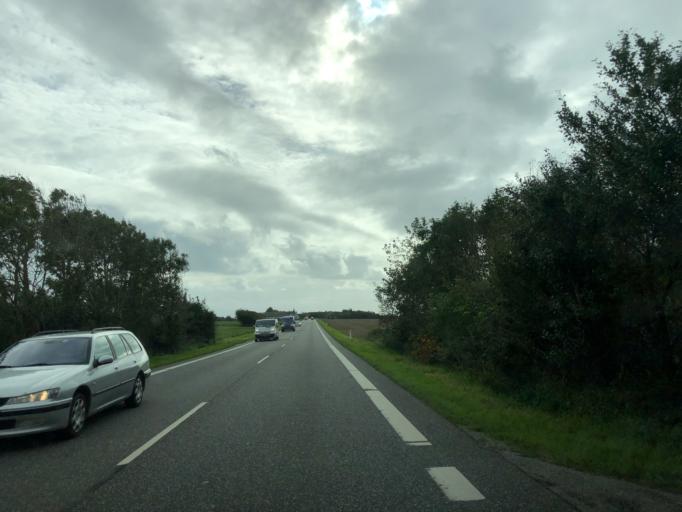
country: DK
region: North Denmark
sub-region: Thisted Kommune
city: Hurup
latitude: 56.6993
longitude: 8.4070
